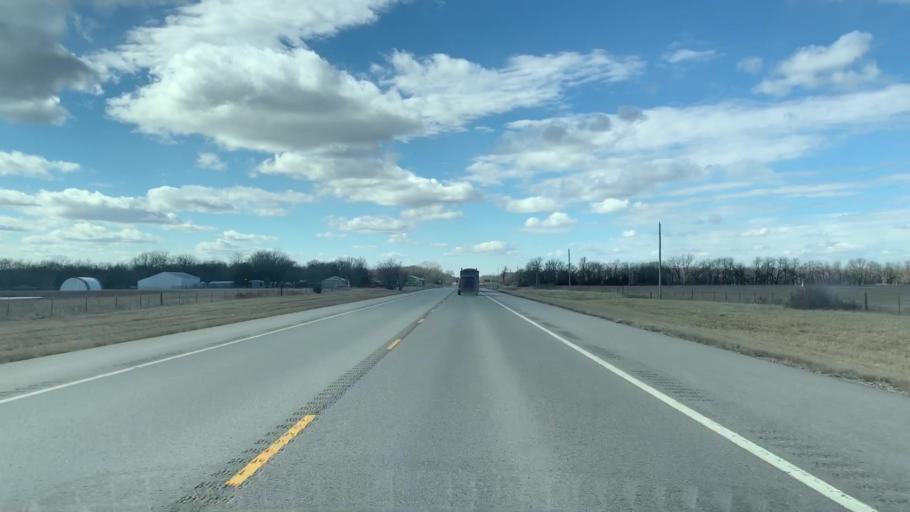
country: US
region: Kansas
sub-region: Cherokee County
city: Columbus
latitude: 37.3401
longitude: -94.9183
